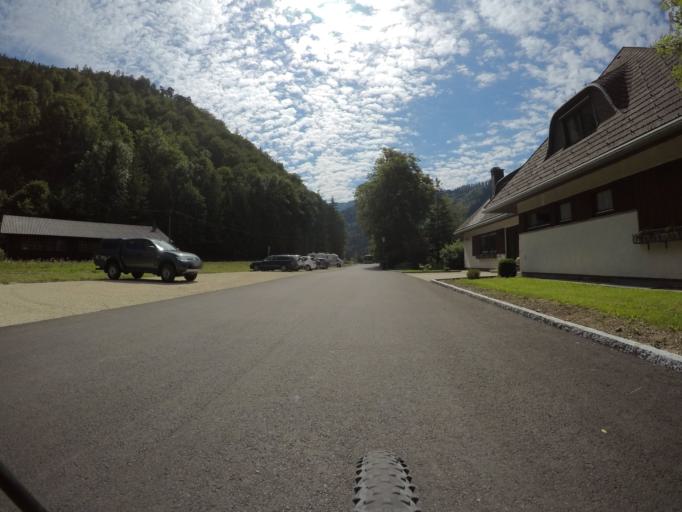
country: AT
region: Lower Austria
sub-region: Politischer Bezirk Amstetten
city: Hollenstein an der Ybbs
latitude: 47.8059
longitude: 14.7719
